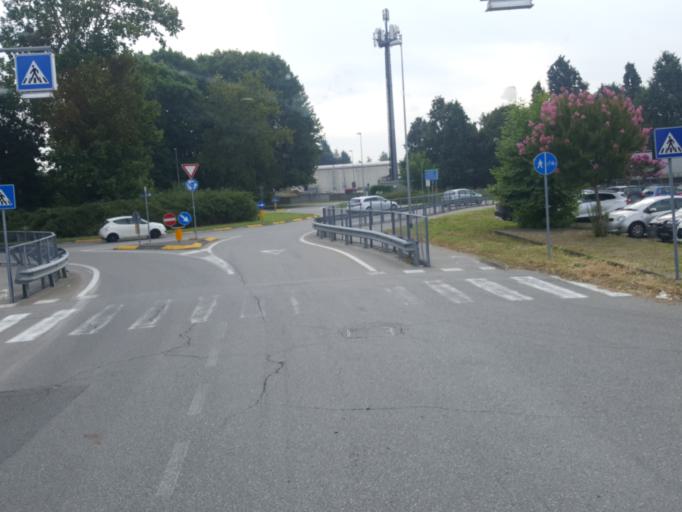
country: IT
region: Lombardy
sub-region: Provincia di Monza e Brianza
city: Cavenago di Brianza
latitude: 45.5802
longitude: 9.4106
